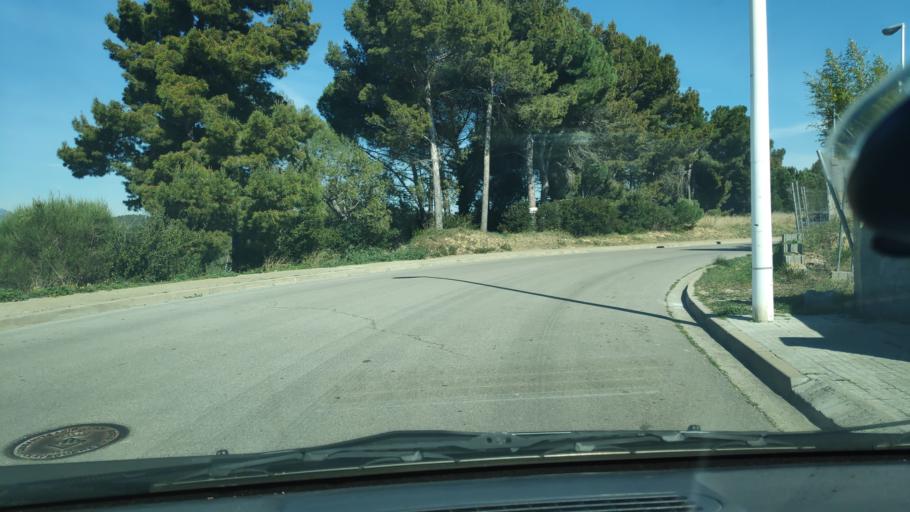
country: ES
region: Catalonia
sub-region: Provincia de Barcelona
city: Rubi
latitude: 41.5068
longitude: 2.0448
